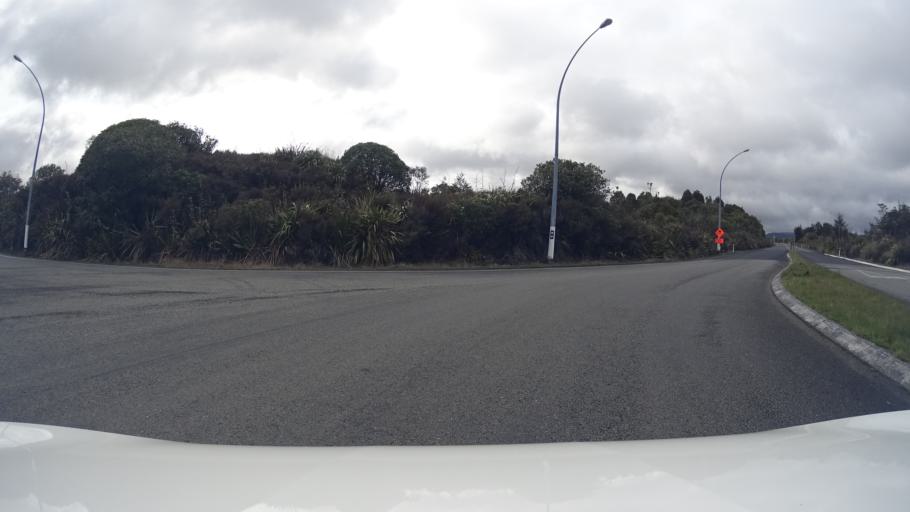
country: NZ
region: Waikato
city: Turangi
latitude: -39.1604
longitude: 175.4931
